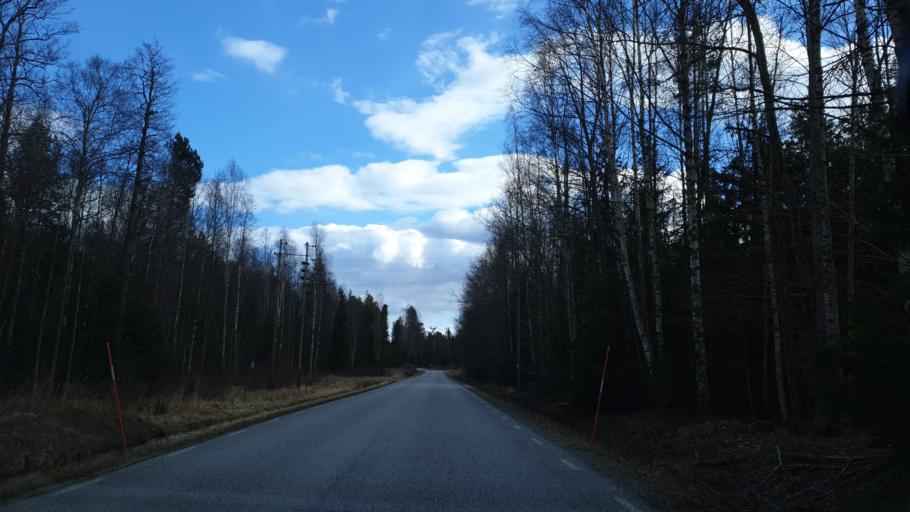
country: SE
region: Stockholm
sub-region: Varmdo Kommun
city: Hemmesta
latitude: 59.2339
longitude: 18.4811
